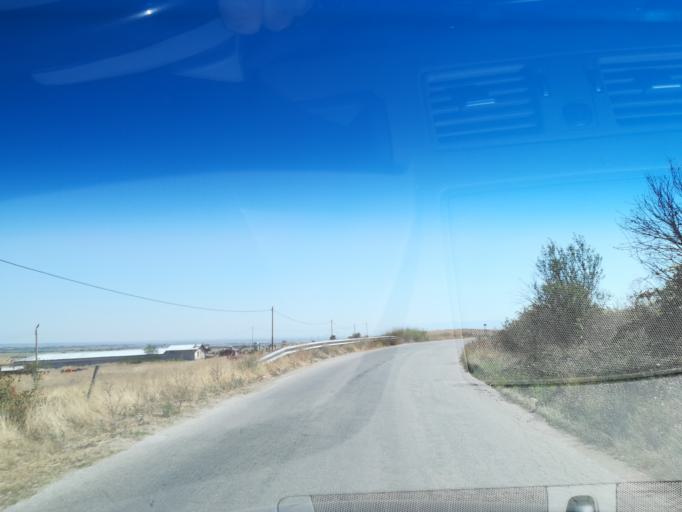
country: BG
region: Pazardzhik
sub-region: Obshtina Pazardzhik
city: Pazardzhik
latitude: 42.3272
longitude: 24.4067
